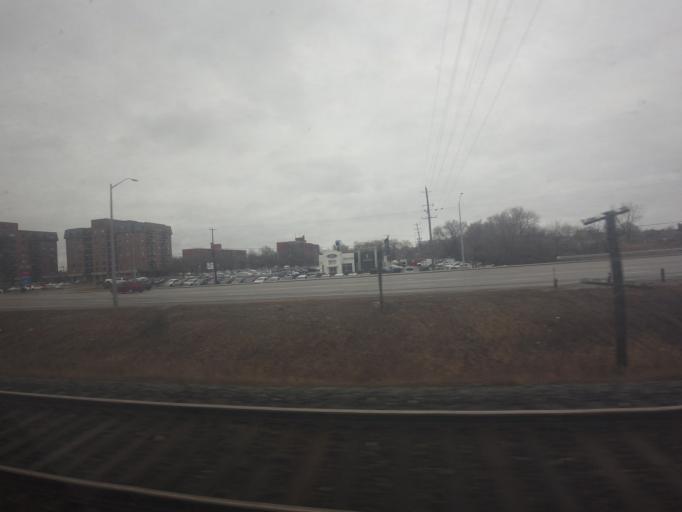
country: CA
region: Ontario
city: Kingston
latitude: 44.2377
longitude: -76.5811
